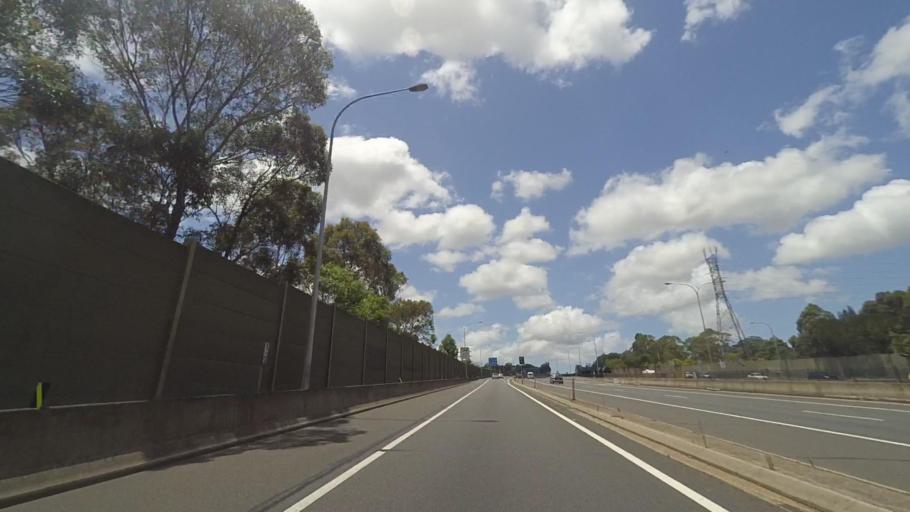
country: AU
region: New South Wales
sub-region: The Hills Shire
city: West Pennant
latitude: -33.7599
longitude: 151.0398
